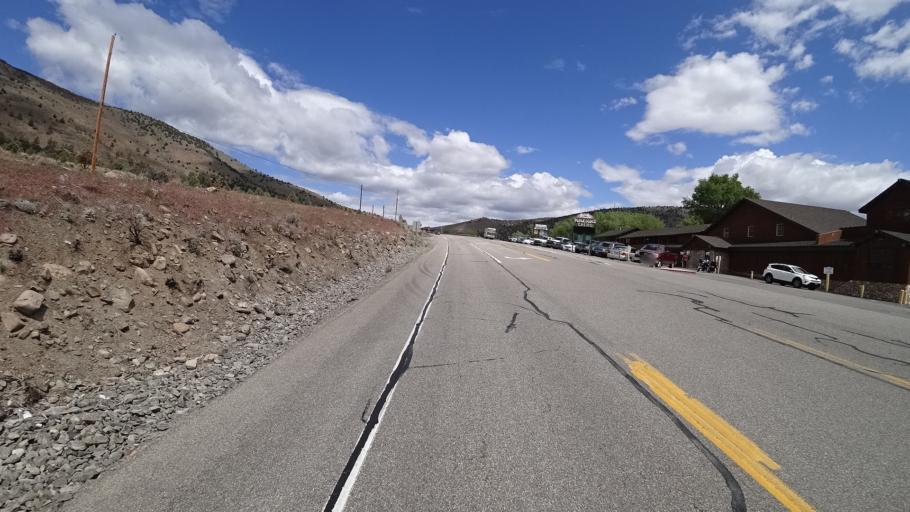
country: US
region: Nevada
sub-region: Lyon County
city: Smith Valley
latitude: 38.6946
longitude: -119.5487
